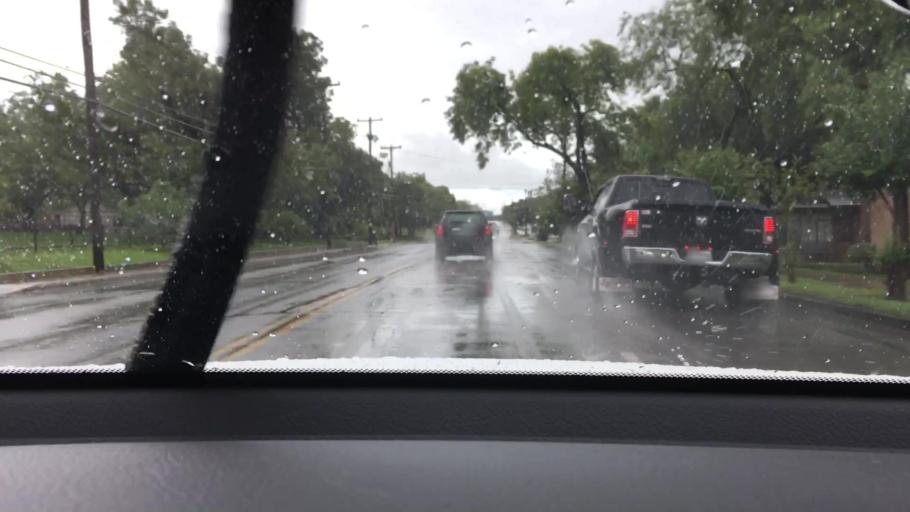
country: US
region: Texas
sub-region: Bexar County
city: Alamo Heights
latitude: 29.4892
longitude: -98.4666
